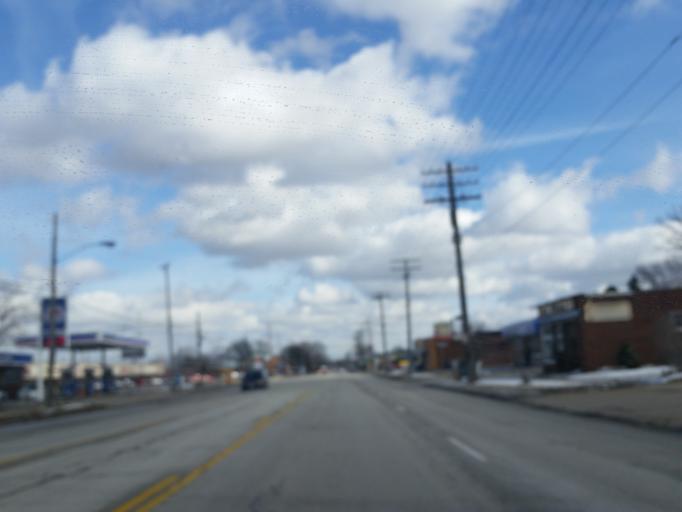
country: US
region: Ohio
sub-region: Cuyahoga County
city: Brooklyn Heights
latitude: 41.4191
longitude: -81.6993
